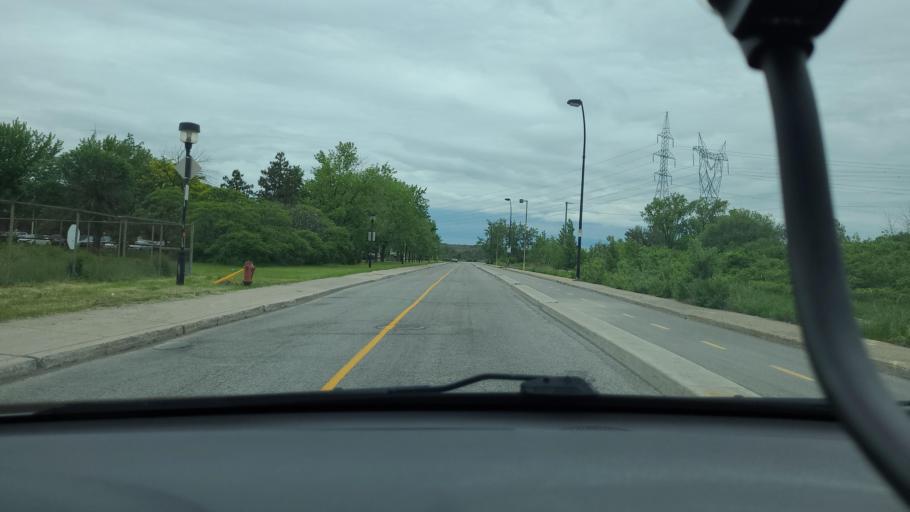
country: CA
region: Quebec
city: Montreal-Est
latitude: 45.6696
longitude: -73.5251
